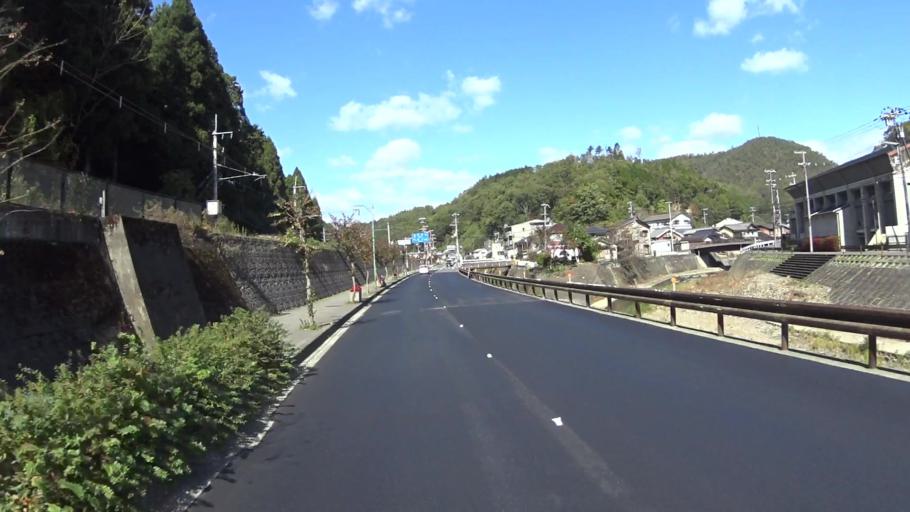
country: JP
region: Kyoto
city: Kameoka
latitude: 35.1596
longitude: 135.5054
